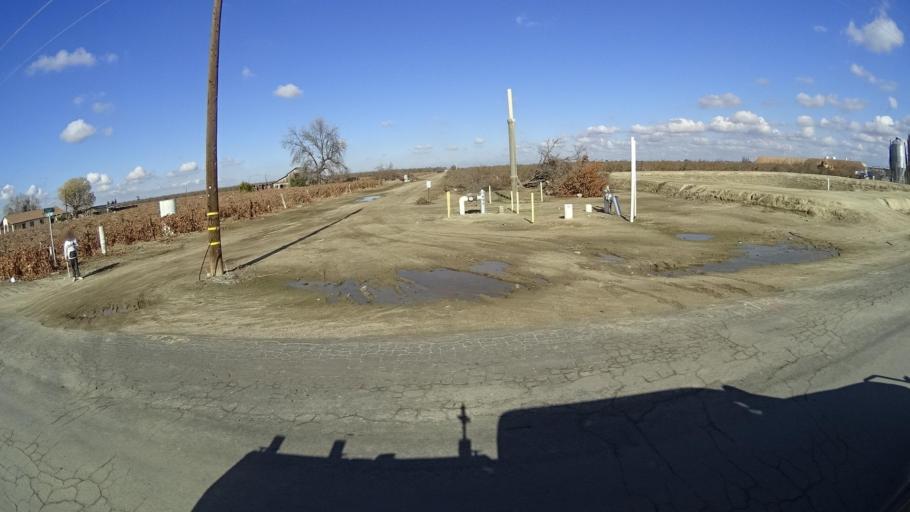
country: US
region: California
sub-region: Kern County
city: McFarland
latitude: 35.6887
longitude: -119.2498
